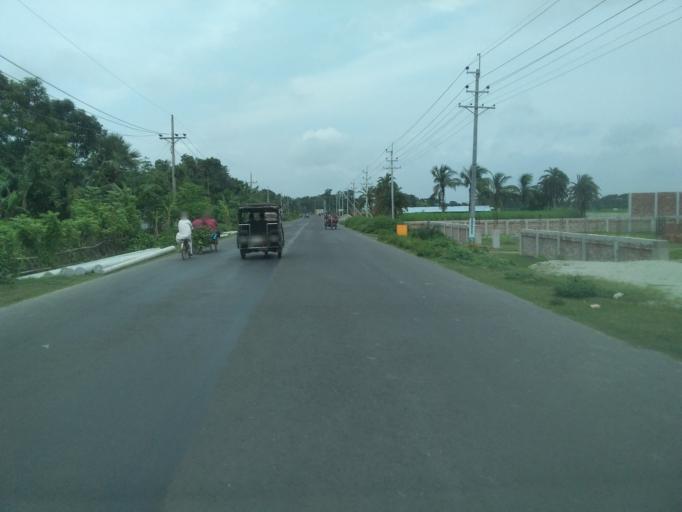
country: BD
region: Khulna
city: Satkhira
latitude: 22.7675
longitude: 89.1464
